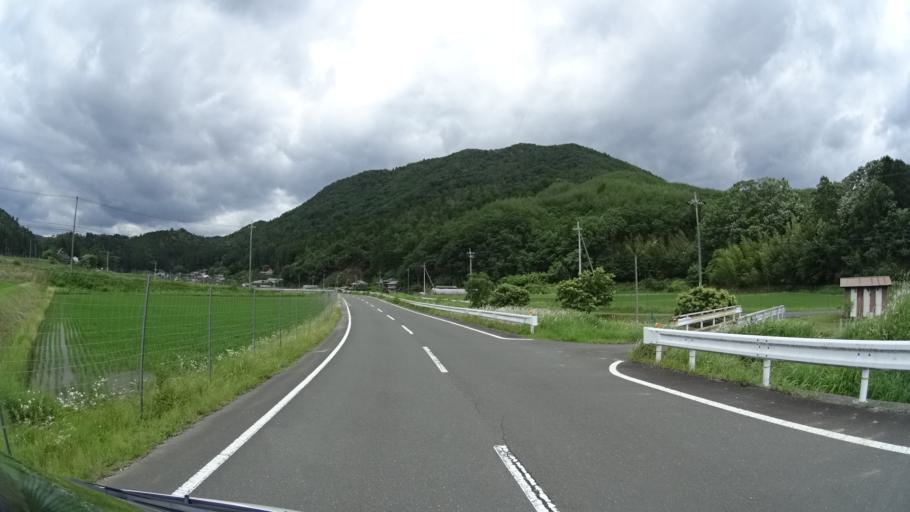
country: JP
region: Kyoto
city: Kameoka
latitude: 35.0502
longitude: 135.4136
